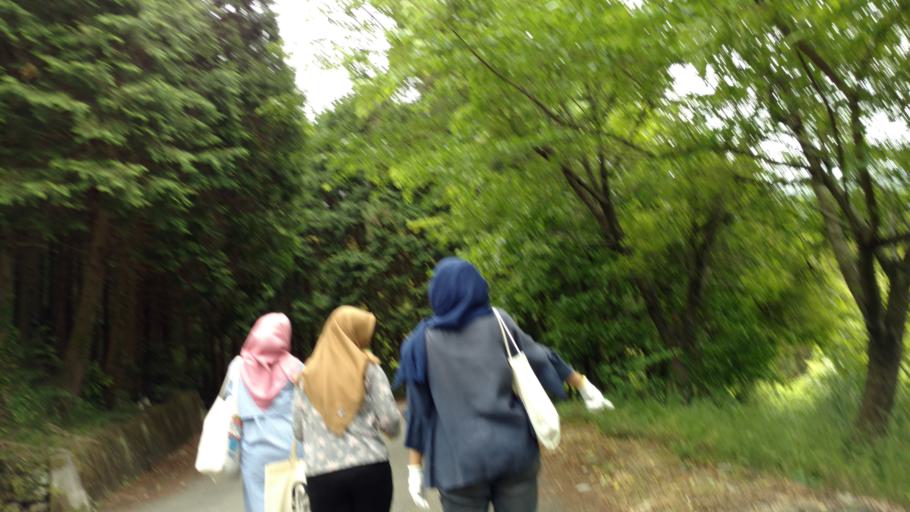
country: JP
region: Ehime
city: Saijo
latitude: 33.8662
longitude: 133.1995
